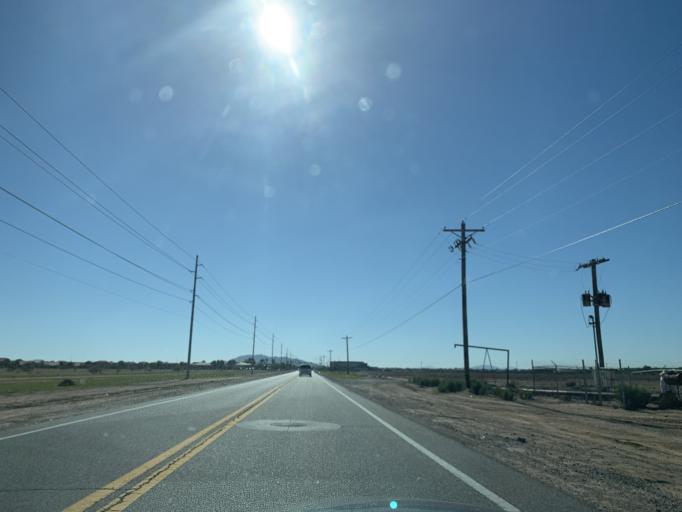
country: US
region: Arizona
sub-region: Pinal County
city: Casa Grande
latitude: 32.9131
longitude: -111.7226
